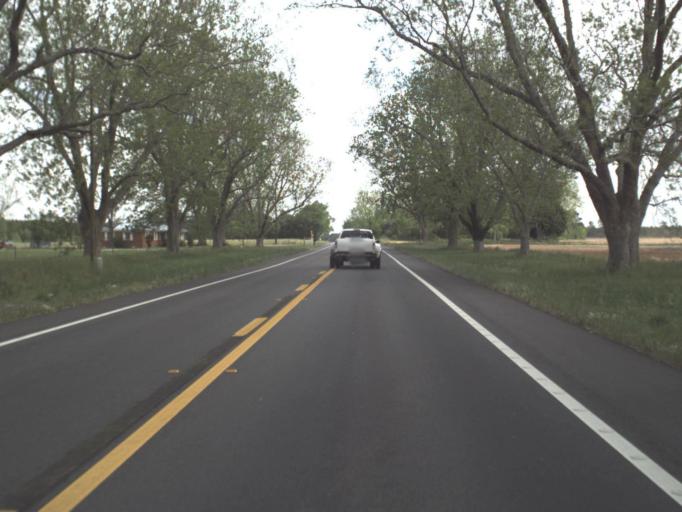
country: US
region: Florida
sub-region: Escambia County
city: Century
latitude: 30.8672
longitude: -87.1570
